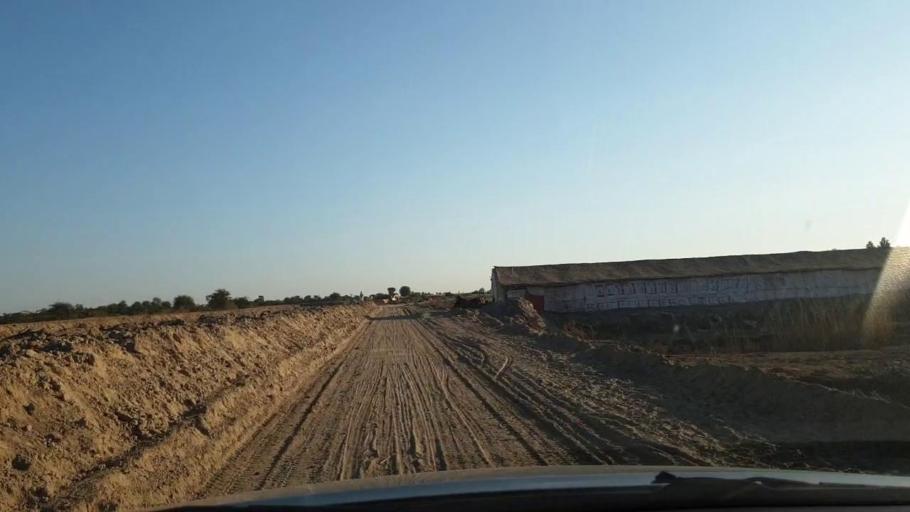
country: PK
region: Sindh
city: Tando Mittha Khan
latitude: 25.8359
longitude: 69.1738
